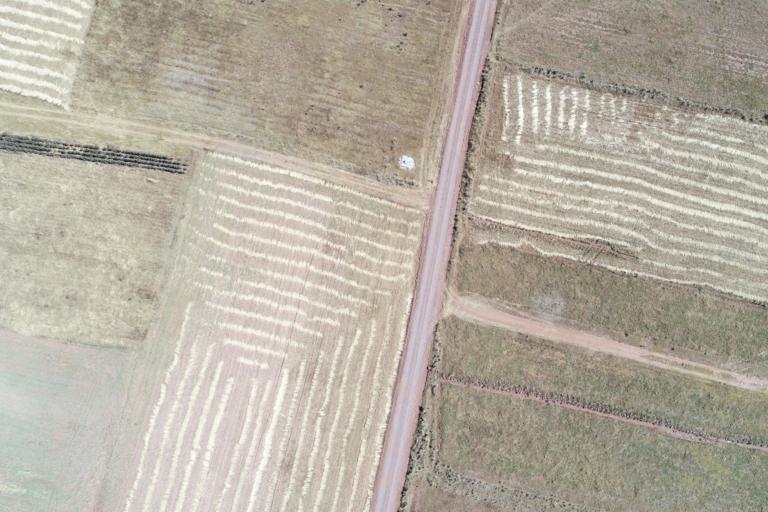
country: BO
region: La Paz
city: Tiahuanaco
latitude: -16.5942
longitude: -68.7743
